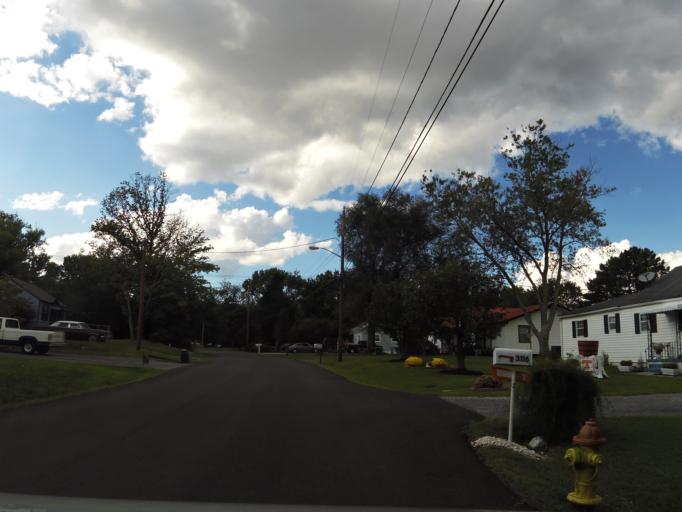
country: US
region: Tennessee
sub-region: Knox County
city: Knoxville
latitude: 36.0161
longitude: -83.8985
